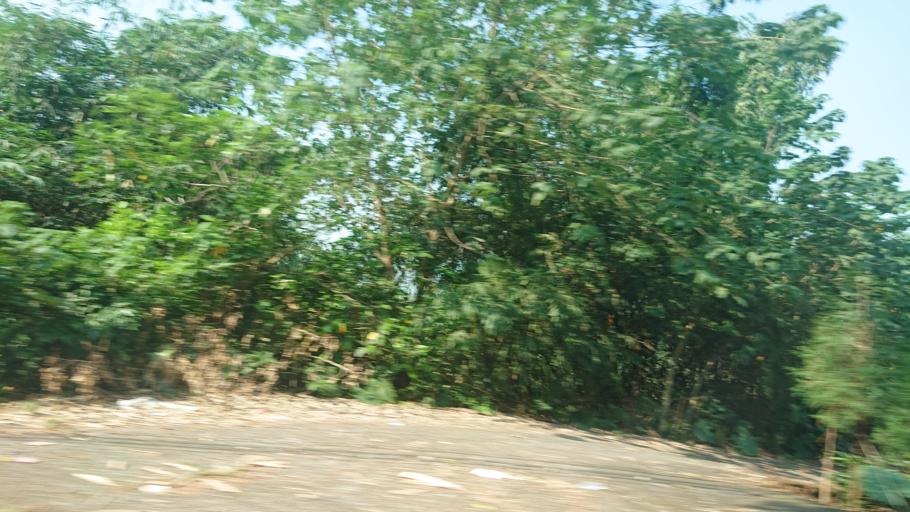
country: TW
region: Taiwan
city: Lugu
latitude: 23.7064
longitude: 120.6636
